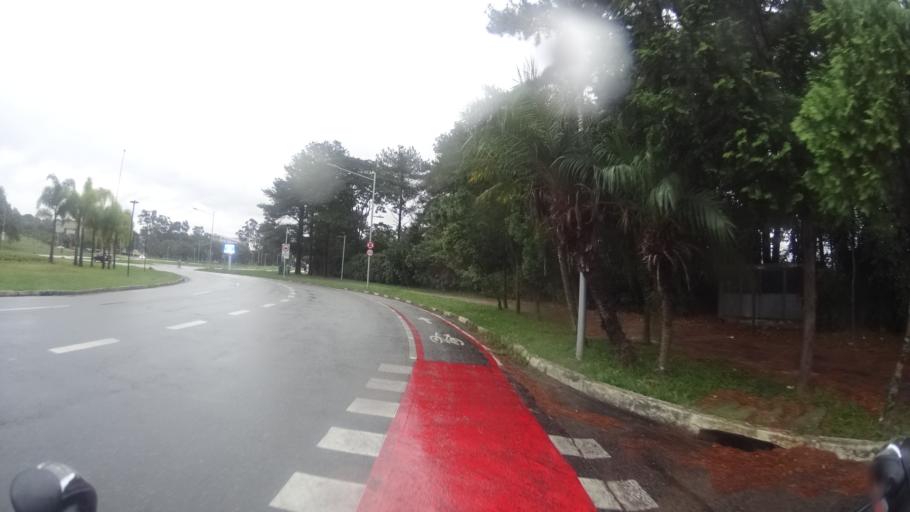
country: BR
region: Sao Paulo
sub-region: Osasco
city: Osasco
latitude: -23.5620
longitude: -46.7184
